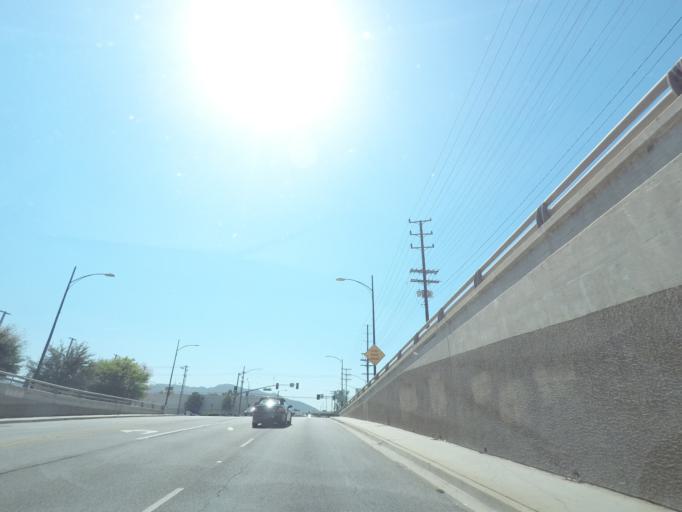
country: US
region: California
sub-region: Los Angeles County
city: Burbank
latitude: 34.1721
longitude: -118.3023
